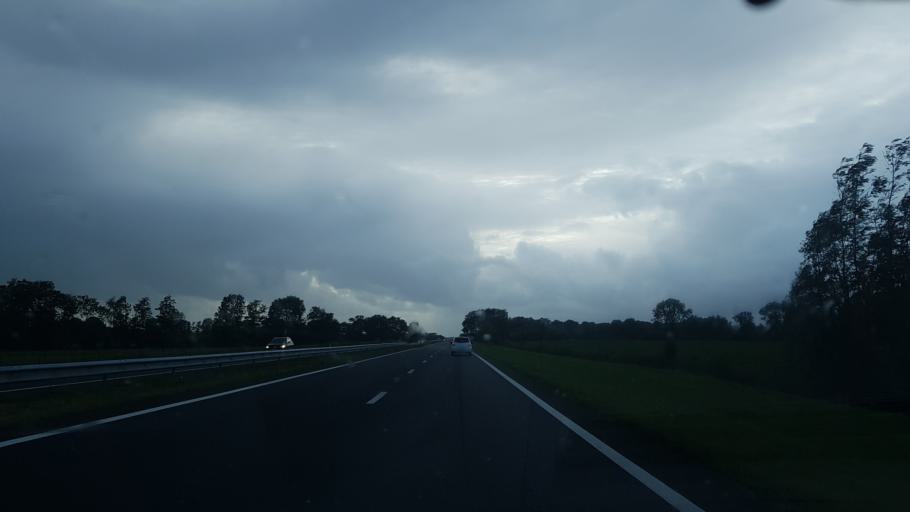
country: NL
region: Friesland
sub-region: Gemeente Tytsjerksteradiel
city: Garyp
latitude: 53.1516
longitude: 5.9776
